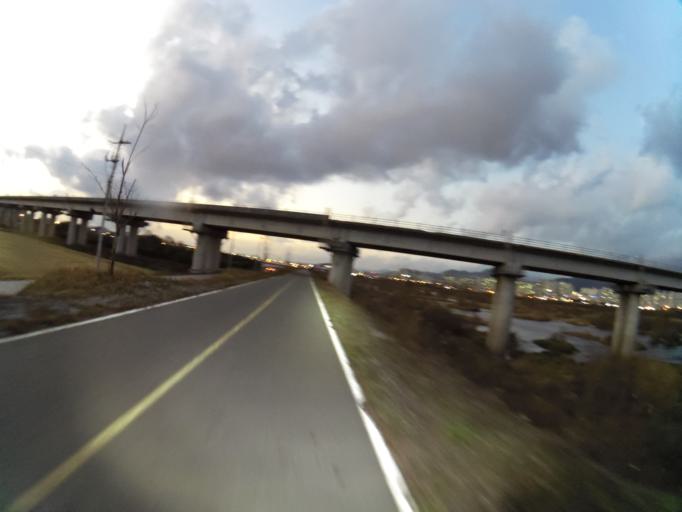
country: KR
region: Gyeongsangbuk-do
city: Gyeongsan-si
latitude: 35.8575
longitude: 128.7251
